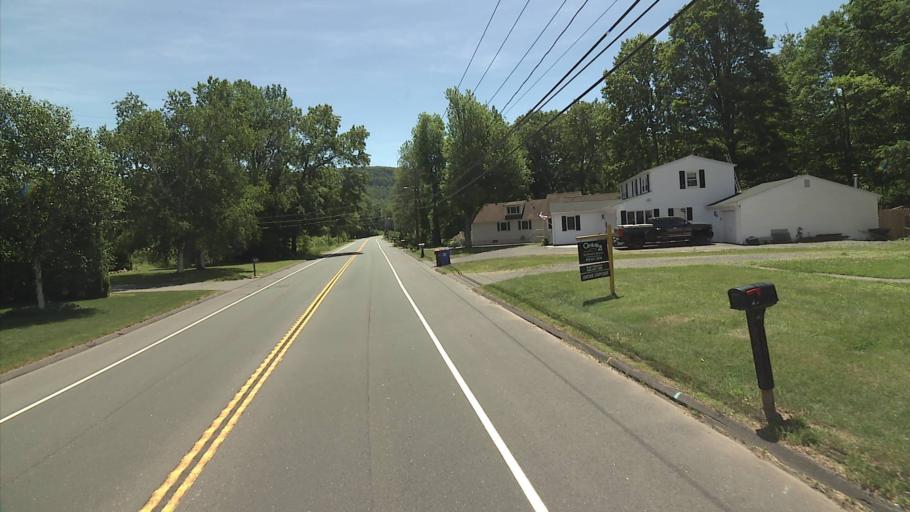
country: US
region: Connecticut
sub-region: New Haven County
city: Meriden
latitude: 41.5720
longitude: -72.8605
